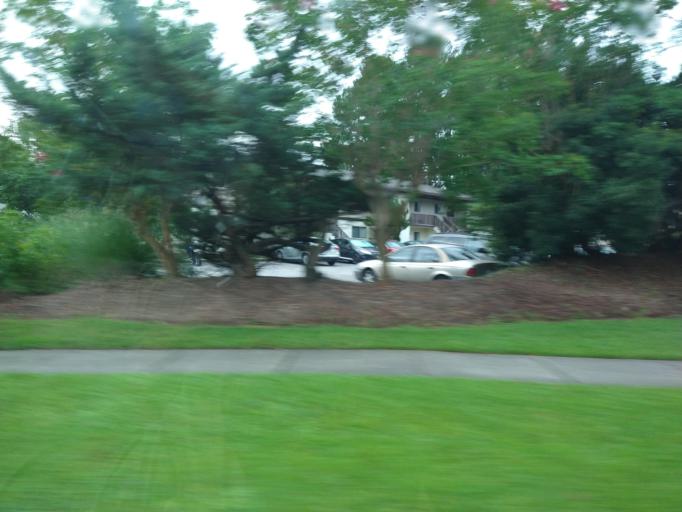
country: US
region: North Carolina
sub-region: Onslow County
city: Pumpkin Center
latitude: 34.7693
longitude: -77.3767
